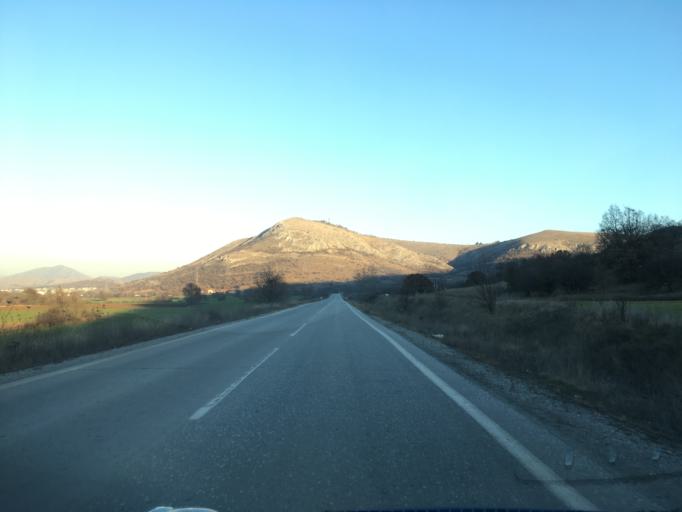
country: GR
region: West Macedonia
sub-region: Nomos Kozanis
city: Kozani
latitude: 40.3172
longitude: 21.7484
